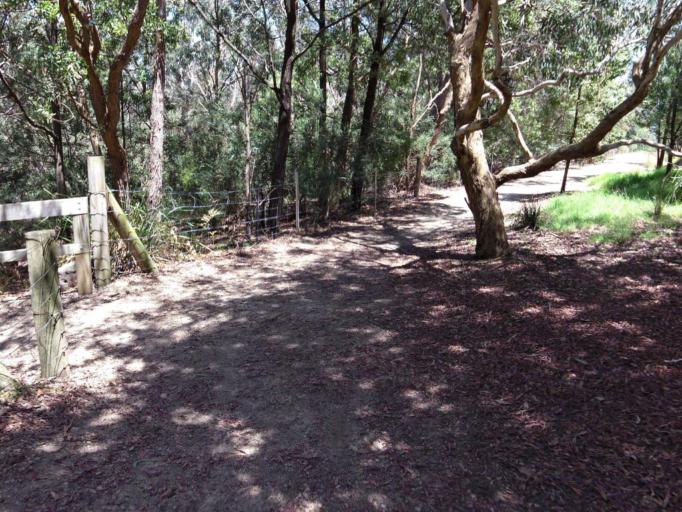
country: AU
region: Victoria
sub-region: Whitehorse
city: Burwood
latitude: -37.8642
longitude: 145.1270
